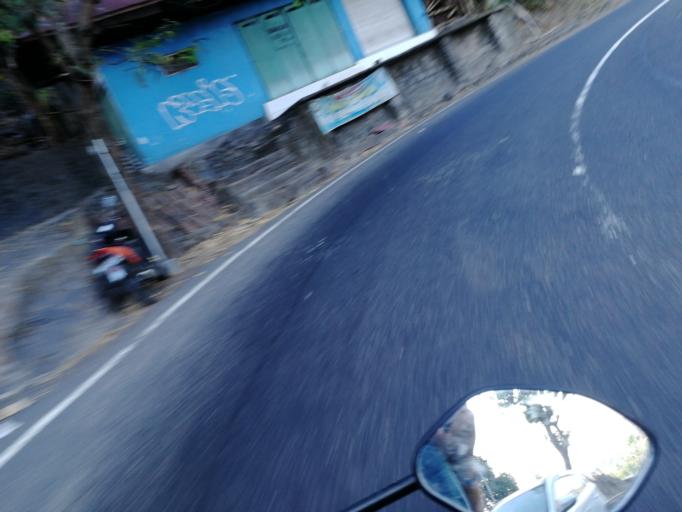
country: ID
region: Bali
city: Banjar Kangkaang
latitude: -8.3674
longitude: 115.6135
